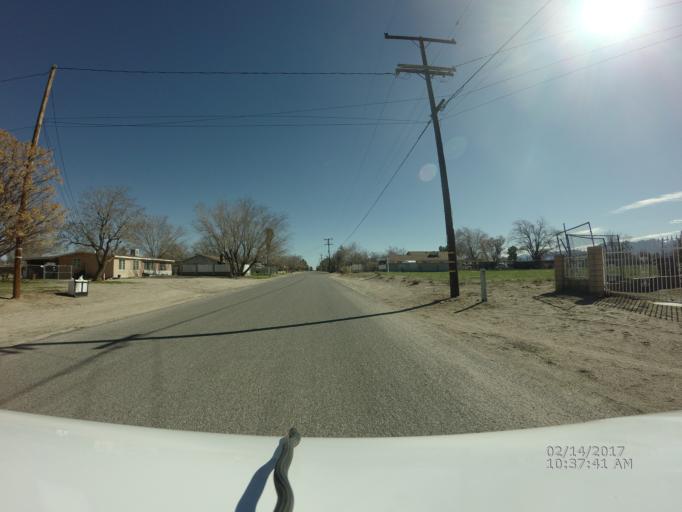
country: US
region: California
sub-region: Los Angeles County
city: Littlerock
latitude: 34.5634
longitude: -117.9458
